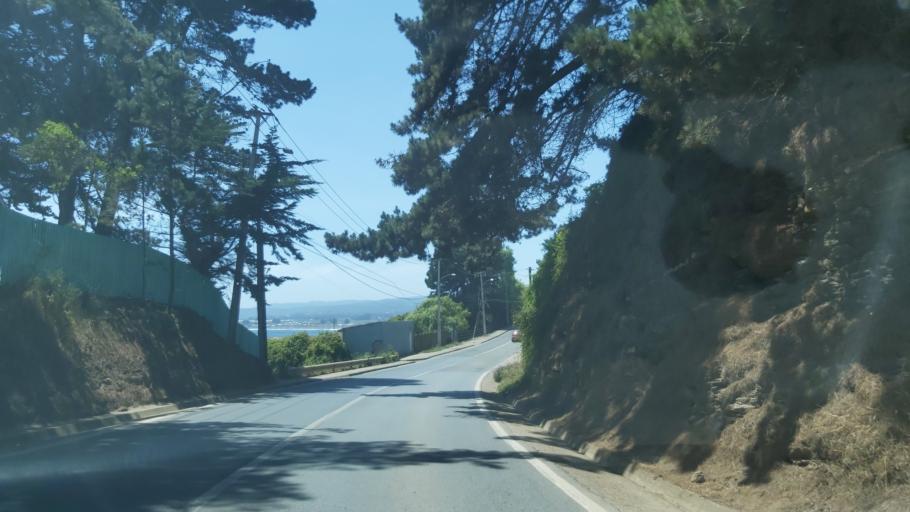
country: CL
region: Maule
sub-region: Provincia de Cauquenes
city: Cauquenes
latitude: -35.8175
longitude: -72.5909
